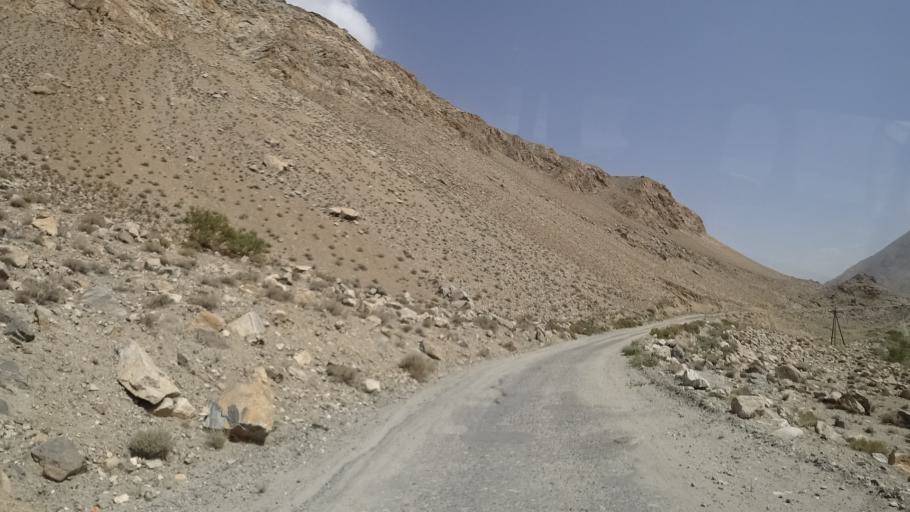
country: TJ
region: Gorno-Badakhshan
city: Ishqoshim
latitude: 36.9383
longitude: 71.4853
